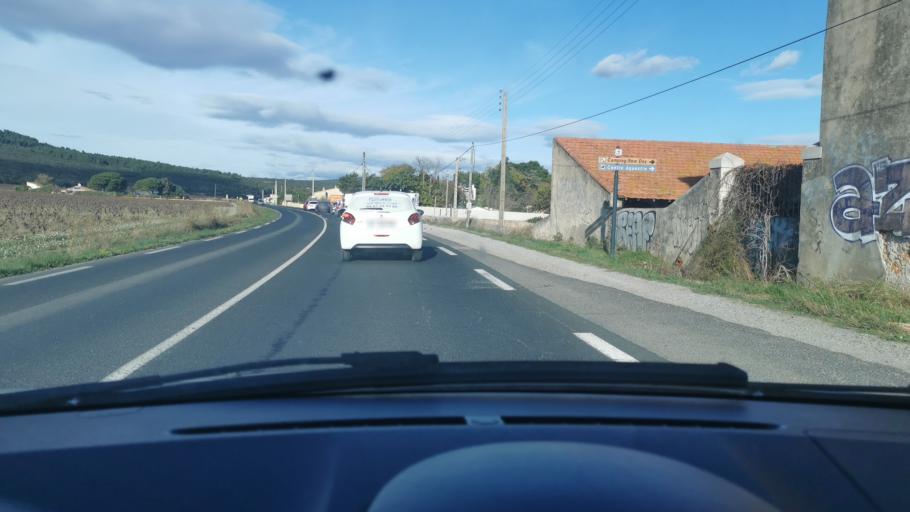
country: FR
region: Languedoc-Roussillon
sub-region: Departement de l'Herault
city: Vic-la-Gardiole
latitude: 43.4804
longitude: 3.7729
